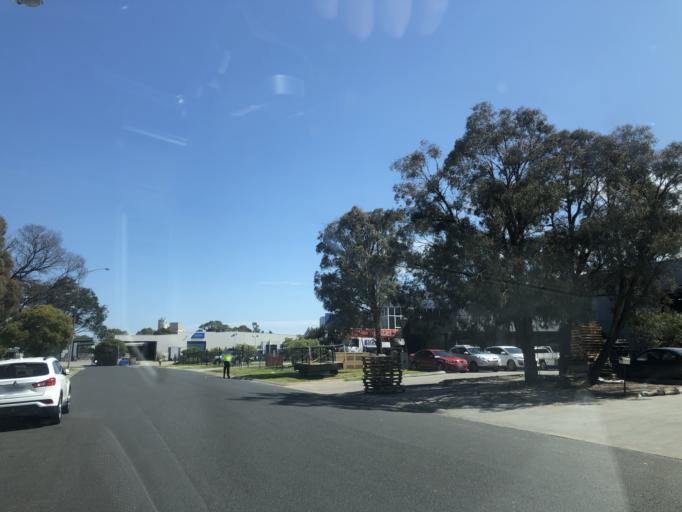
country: AU
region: Victoria
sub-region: Casey
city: Hampton Park
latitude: -38.0313
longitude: 145.2401
